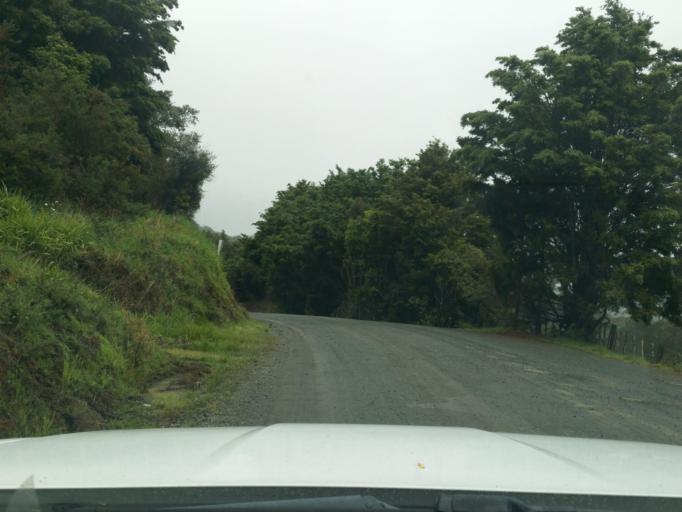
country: NZ
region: Northland
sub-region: Kaipara District
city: Dargaville
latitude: -35.7348
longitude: 173.9084
